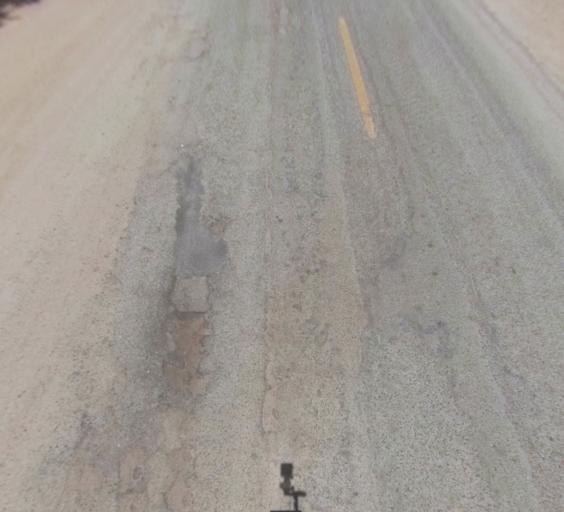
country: US
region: California
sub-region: Madera County
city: Parksdale
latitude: 36.9424
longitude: -120.0209
